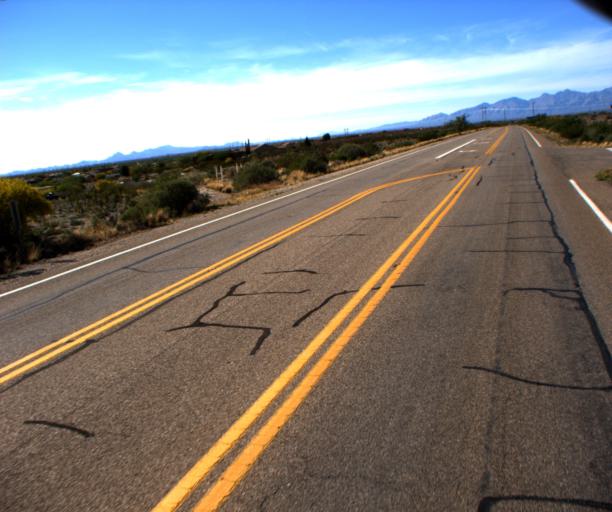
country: US
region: Arizona
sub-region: Pima County
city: Vail
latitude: 31.9991
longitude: -110.6874
